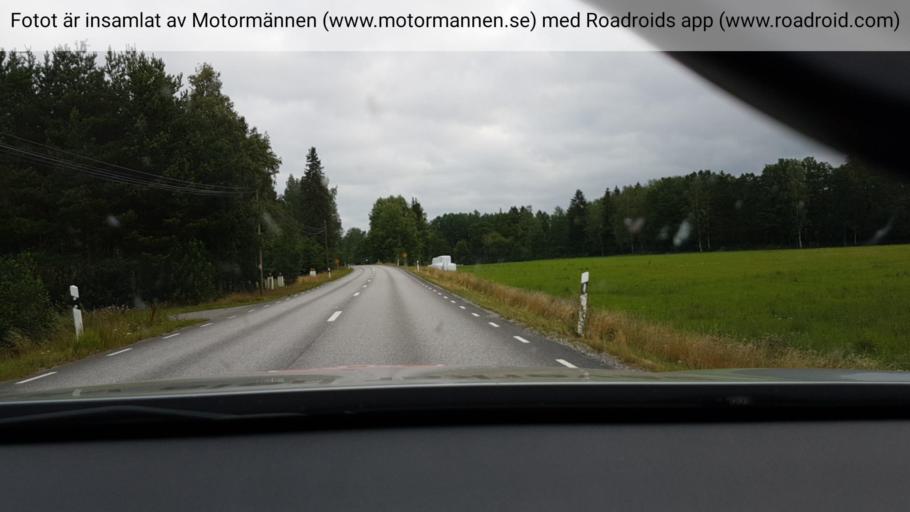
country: SE
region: Stockholm
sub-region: Norrtalje Kommun
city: Skanninge
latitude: 59.8479
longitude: 18.4448
